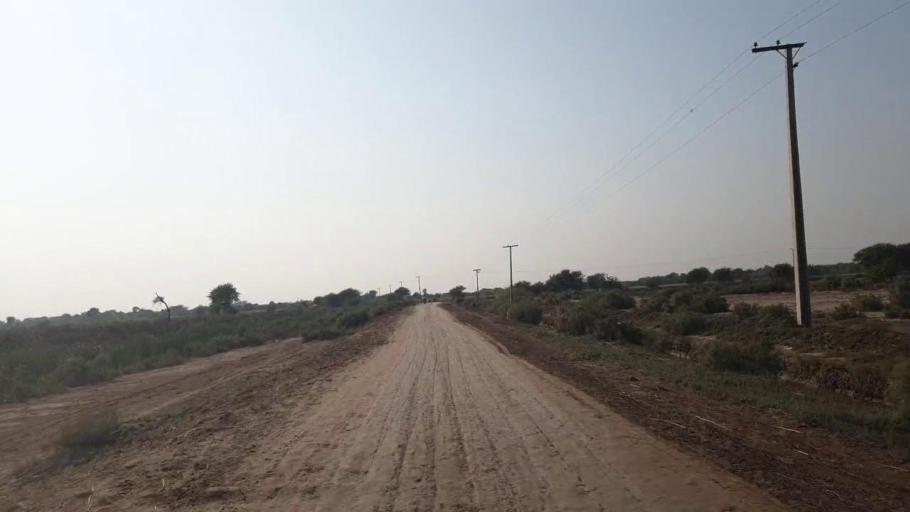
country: PK
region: Sindh
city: Kario
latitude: 24.8912
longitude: 68.6257
